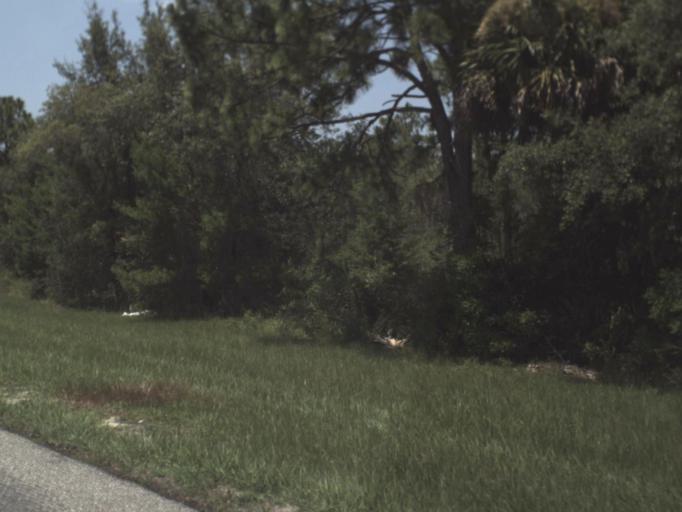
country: US
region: Florida
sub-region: Citrus County
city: Sugarmill Woods
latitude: 28.6727
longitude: -82.5525
